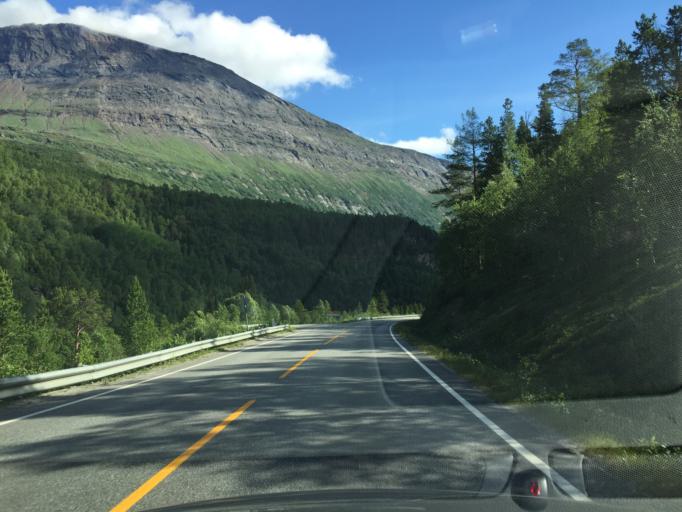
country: NO
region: Nordland
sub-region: Saltdal
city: Rognan
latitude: 66.8241
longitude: 15.4941
